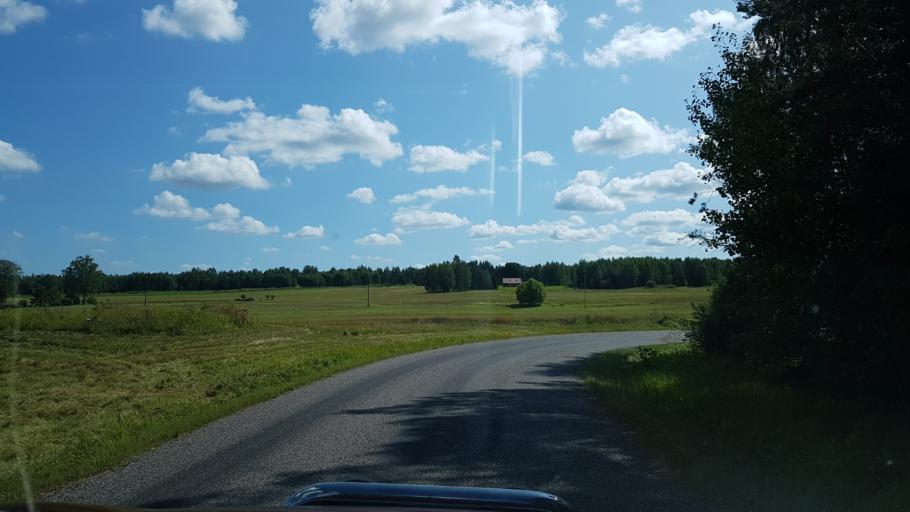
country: EE
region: Vorumaa
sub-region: Voru linn
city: Voru
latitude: 57.7264
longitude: 27.2111
